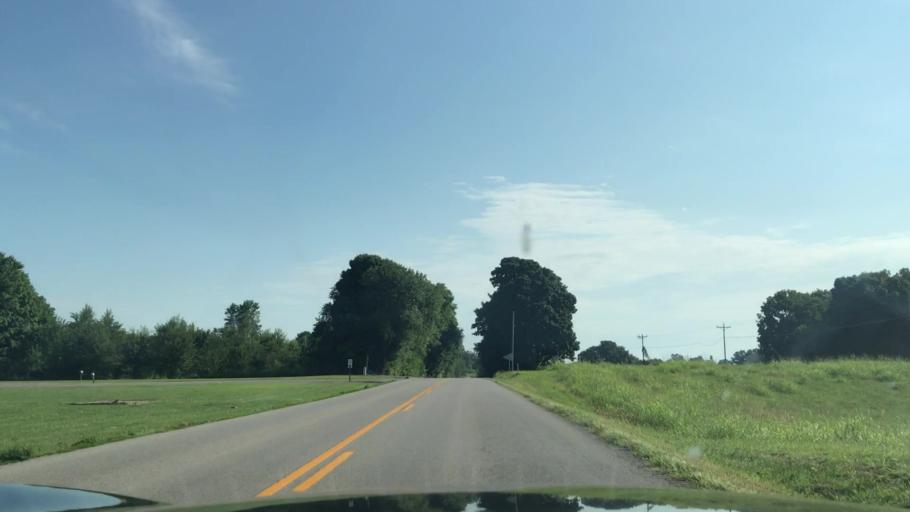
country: US
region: Kentucky
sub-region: Hart County
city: Horse Cave
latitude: 37.1706
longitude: -85.7943
